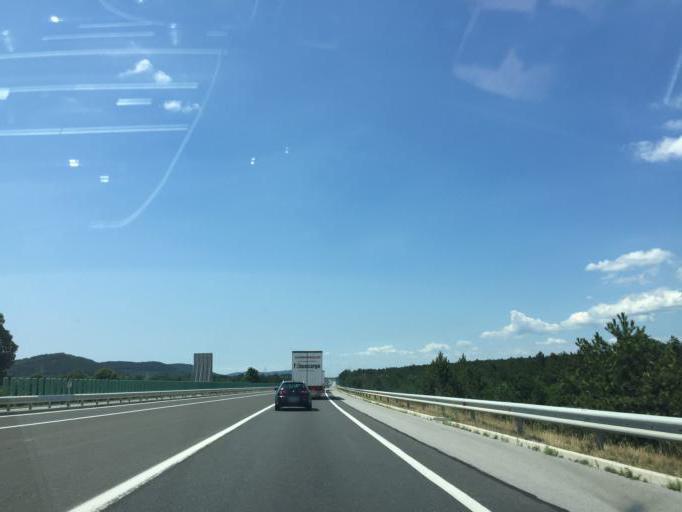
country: SI
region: Divaca
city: Divaca
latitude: 45.6949
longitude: 13.9676
